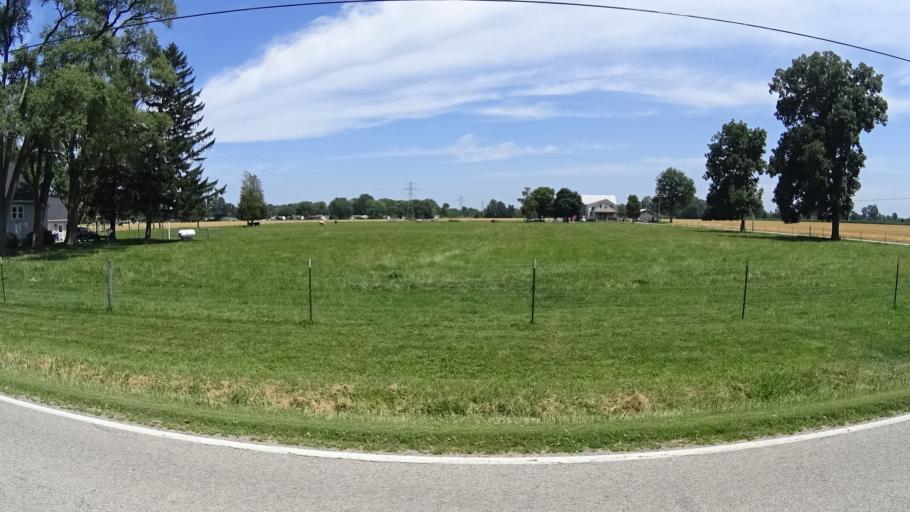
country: US
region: Ohio
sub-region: Erie County
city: Sandusky
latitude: 41.4336
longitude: -82.7724
